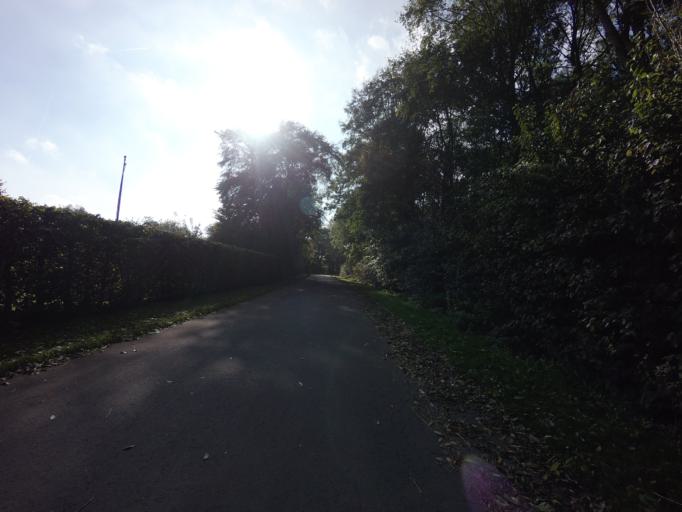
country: NL
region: Utrecht
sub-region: Gemeente Vianen
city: Vianen
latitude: 51.9838
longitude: 5.1321
